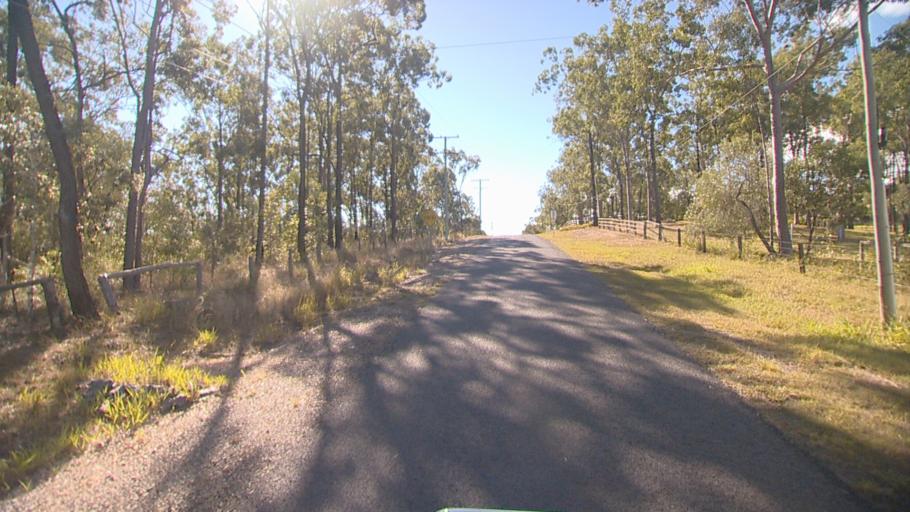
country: AU
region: Queensland
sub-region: Logan
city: Chambers Flat
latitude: -27.8162
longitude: 153.0774
